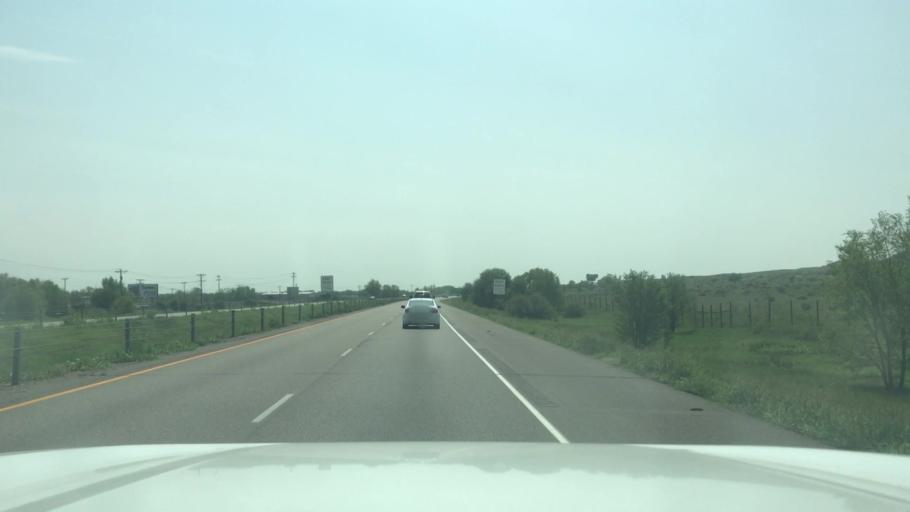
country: US
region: Colorado
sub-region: El Paso County
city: Fountain
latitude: 38.6666
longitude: -104.7044
